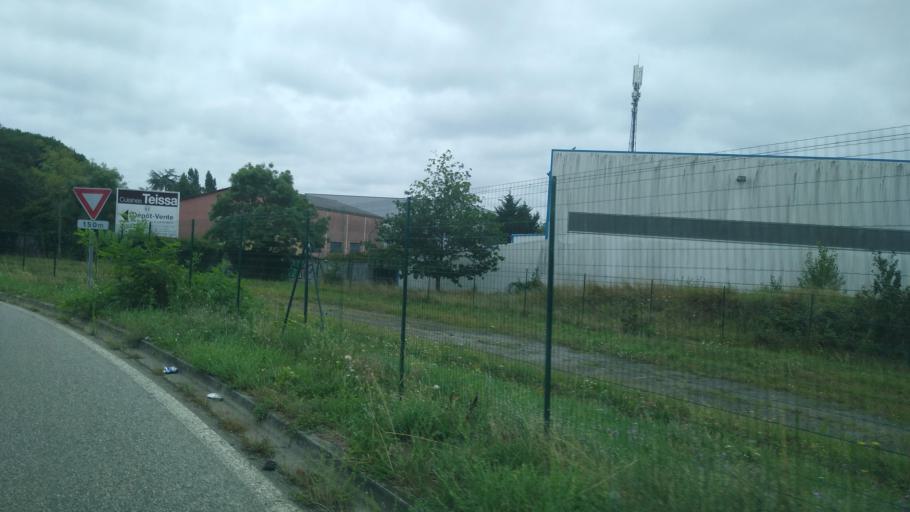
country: FR
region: Midi-Pyrenees
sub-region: Departement de la Haute-Garonne
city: Colomiers
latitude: 43.5964
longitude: 1.3645
